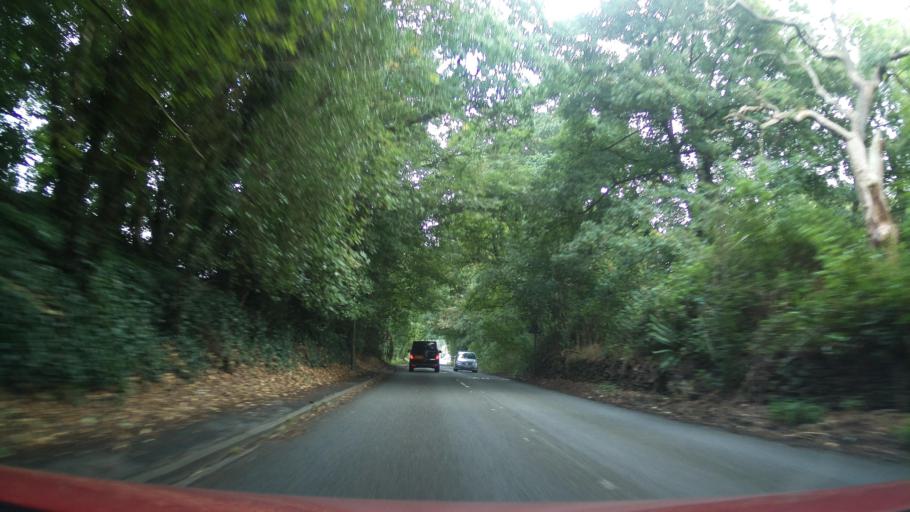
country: GB
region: England
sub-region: Staffordshire
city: Newcastle under Lyme
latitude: 52.9720
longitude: -2.2109
